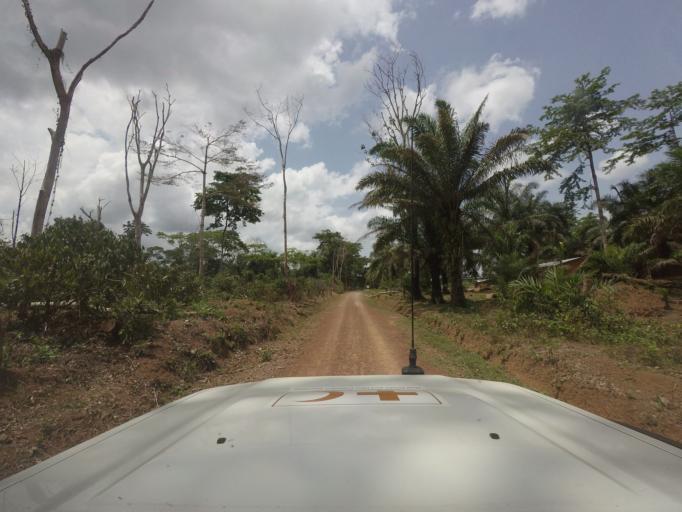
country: GN
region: Nzerekore
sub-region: Yomou
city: Yomou
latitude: 7.2806
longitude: -9.1845
